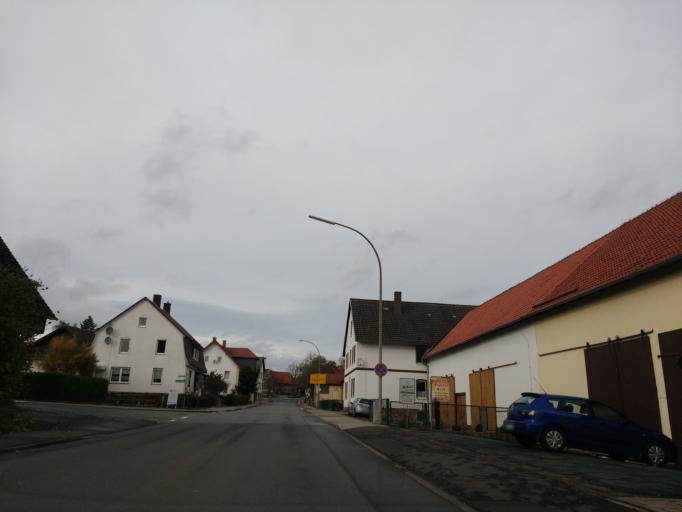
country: DE
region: Hesse
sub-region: Regierungsbezirk Kassel
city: Sachsenhausen
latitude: 51.2417
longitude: 9.0107
